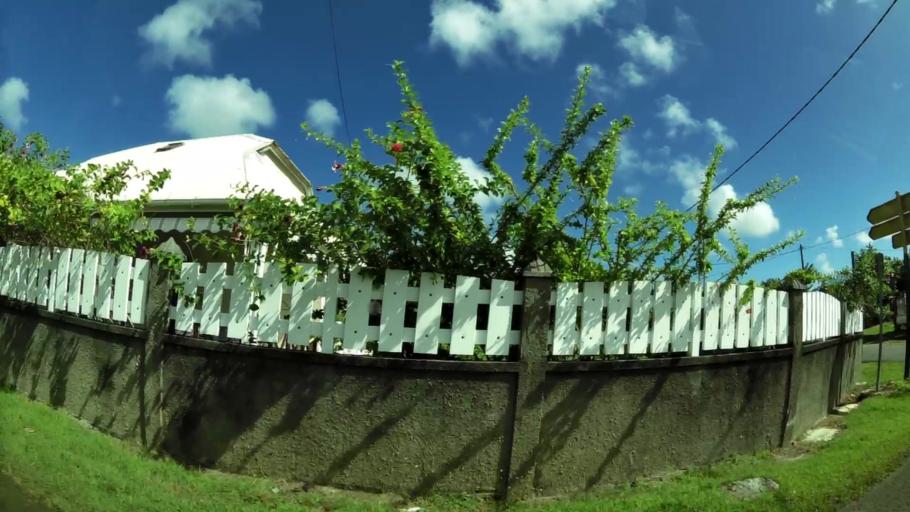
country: GP
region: Guadeloupe
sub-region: Guadeloupe
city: Anse-Bertrand
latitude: 16.4702
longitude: -61.5035
